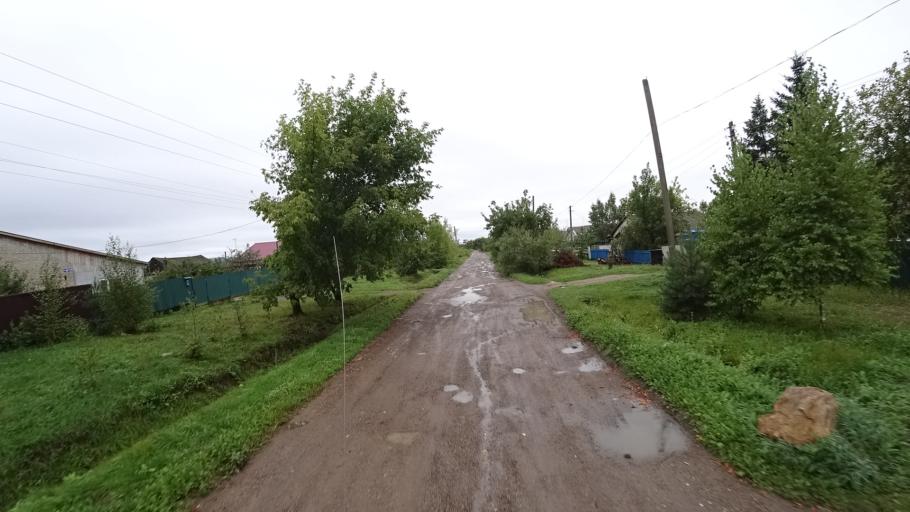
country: RU
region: Primorskiy
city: Monastyrishche
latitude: 44.2323
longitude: 132.4610
